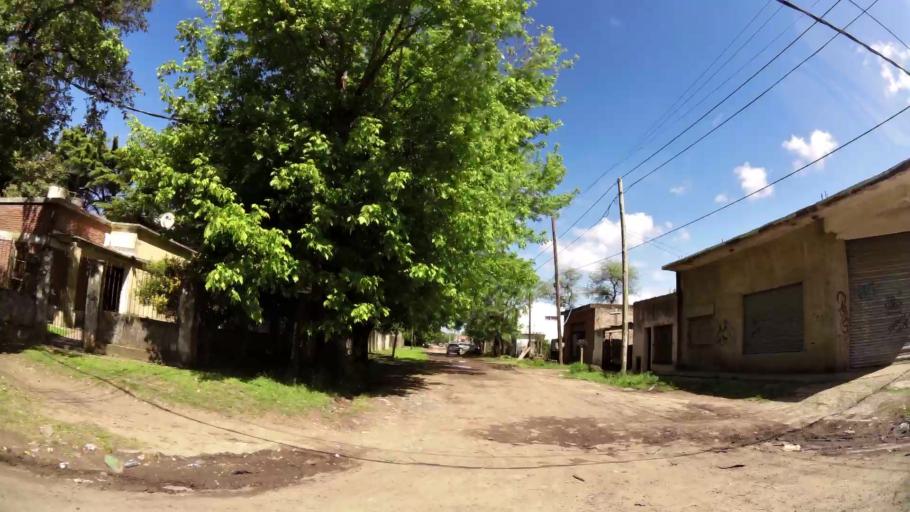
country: AR
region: Buenos Aires
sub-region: Partido de Quilmes
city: Quilmes
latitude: -34.8141
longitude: -58.2621
